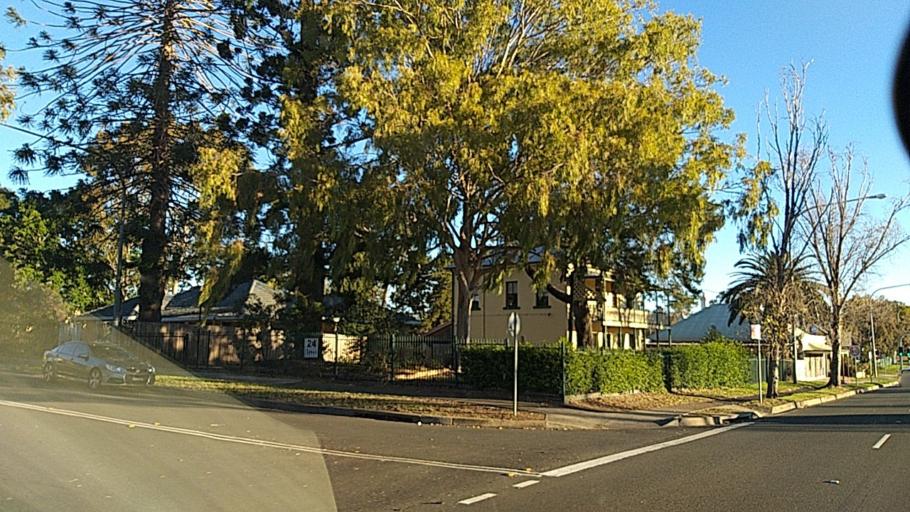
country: AU
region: New South Wales
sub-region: Campbelltown Municipality
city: Campbelltown
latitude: -34.0686
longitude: 150.8153
